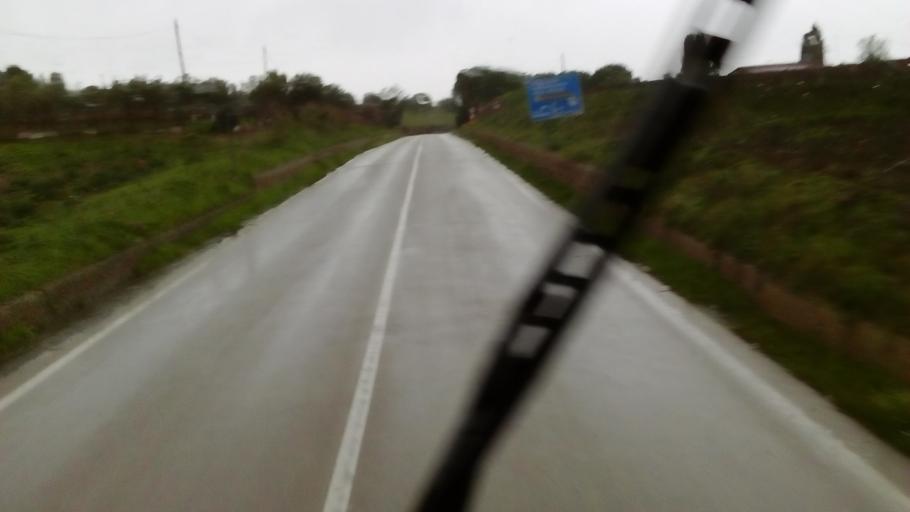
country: IT
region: Sicily
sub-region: Enna
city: Pietraperzia
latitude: 37.4312
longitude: 14.1696
